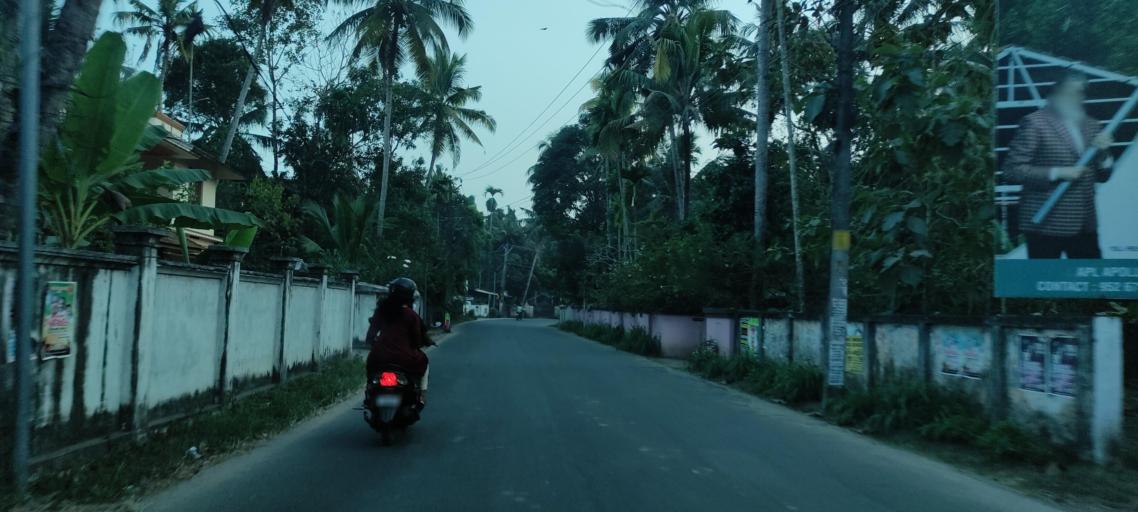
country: IN
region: Kerala
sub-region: Alappuzha
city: Kayankulam
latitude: 9.1249
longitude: 76.4961
